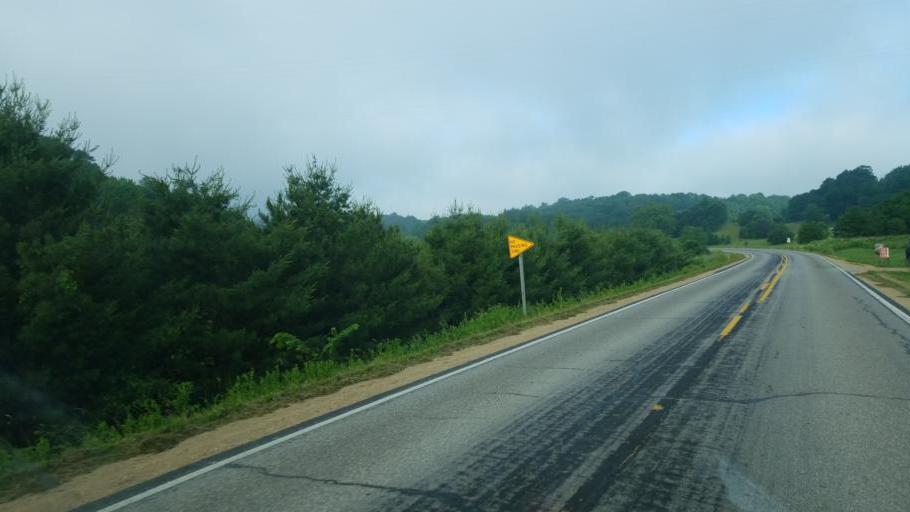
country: US
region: Wisconsin
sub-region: Vernon County
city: Hillsboro
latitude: 43.6453
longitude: -90.4309
